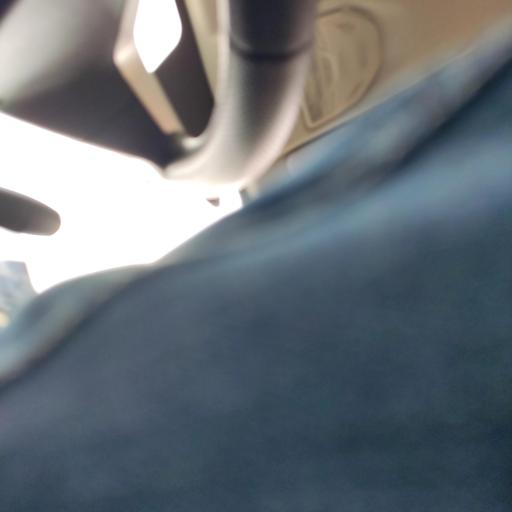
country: RU
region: Samara
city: Smyshlyayevka
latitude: 53.2223
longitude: 50.3456
